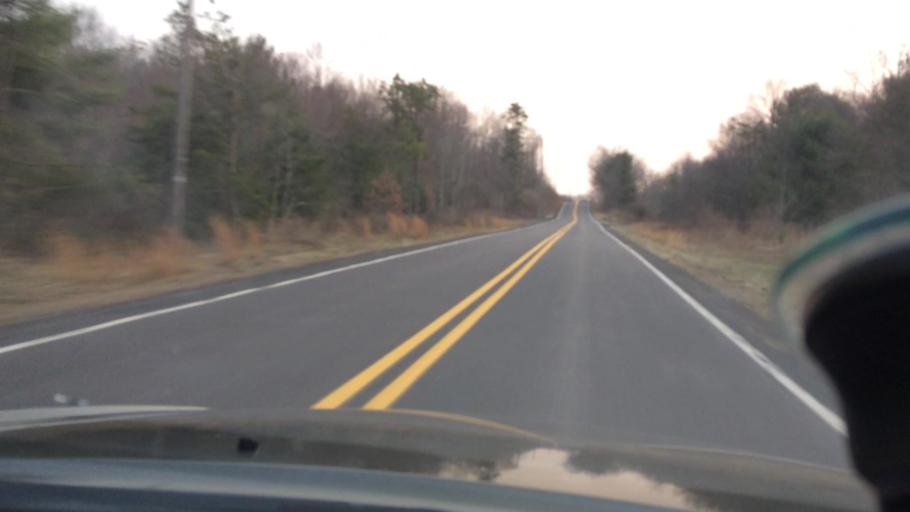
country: US
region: Pennsylvania
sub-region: Luzerne County
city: Freeland
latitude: 41.0824
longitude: -75.8995
